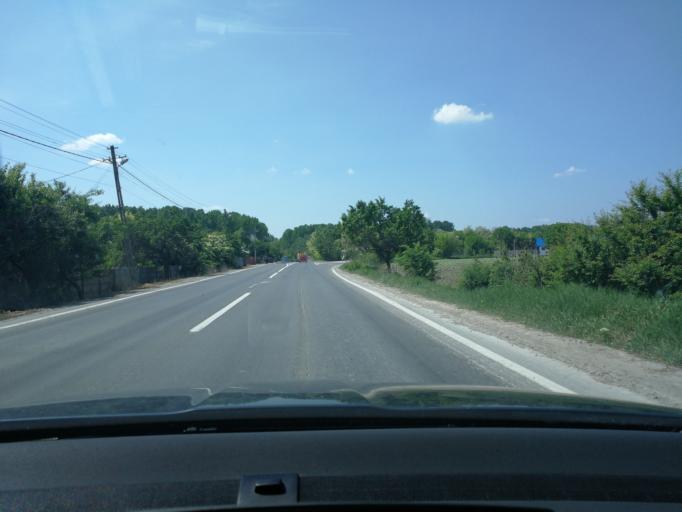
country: RO
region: Prahova
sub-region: Comuna Targsoru Vechi
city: Targsoru Vechi
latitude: 44.8571
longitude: 25.9241
